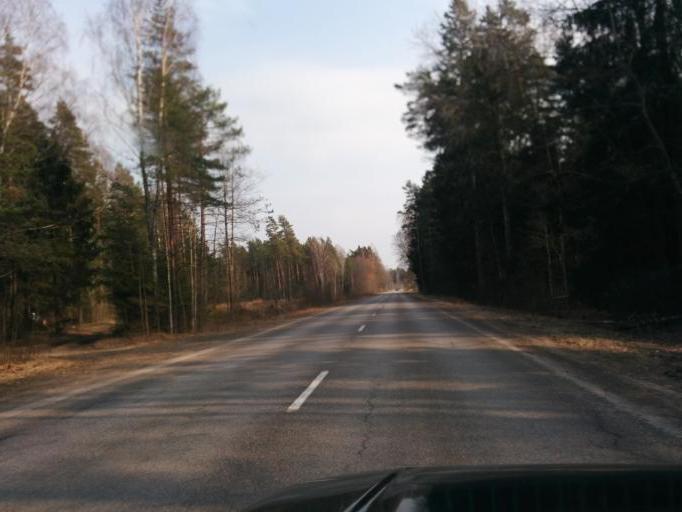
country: LV
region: Kekava
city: Balozi
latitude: 56.7849
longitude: 24.0833
